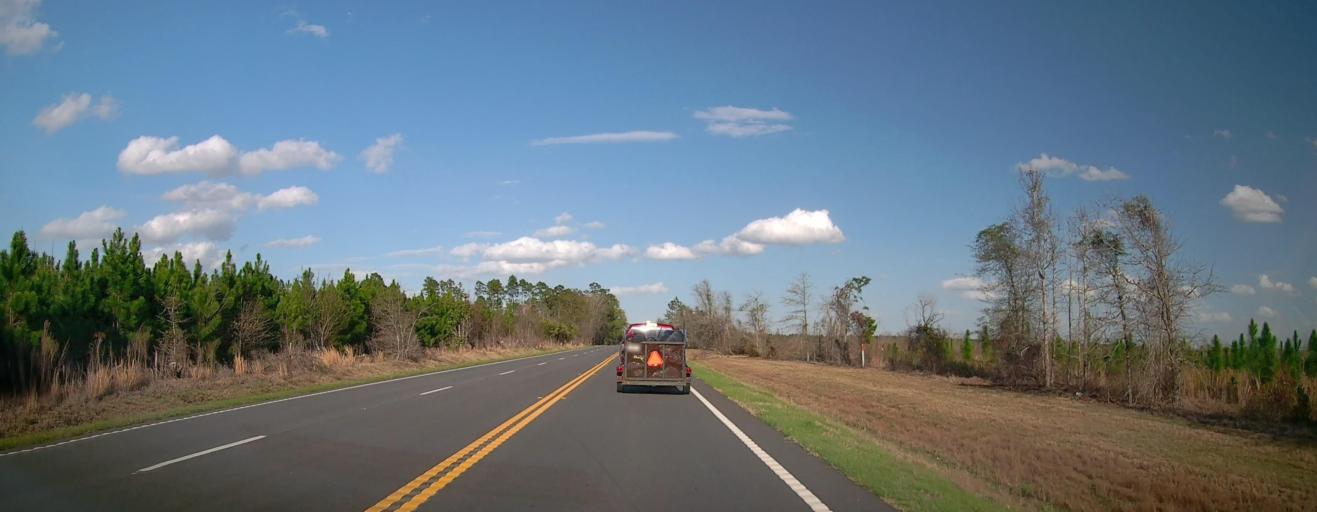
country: US
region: Georgia
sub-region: Montgomery County
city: Mount Vernon
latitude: 32.1912
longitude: -82.5202
